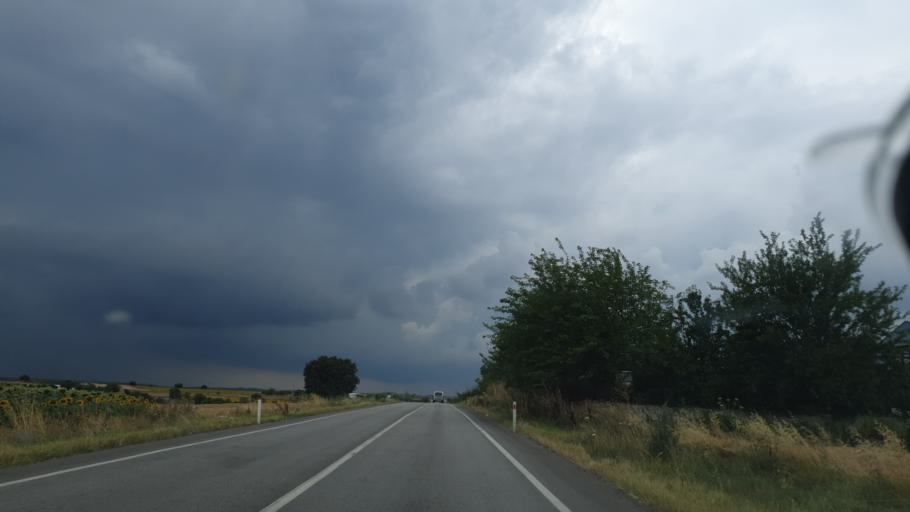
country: TR
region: Tekirdag
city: Hayrabolu
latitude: 41.2189
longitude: 27.0796
